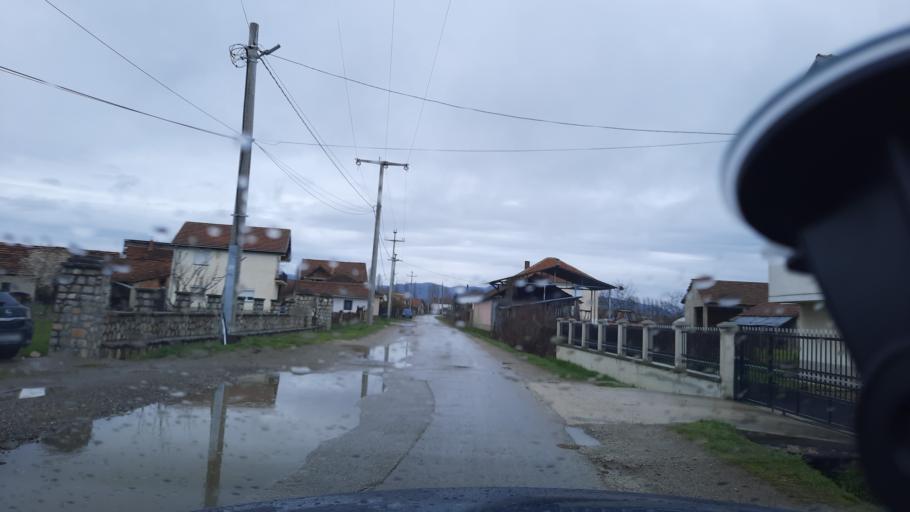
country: MK
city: Misleshevo
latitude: 41.2011
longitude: 20.6932
